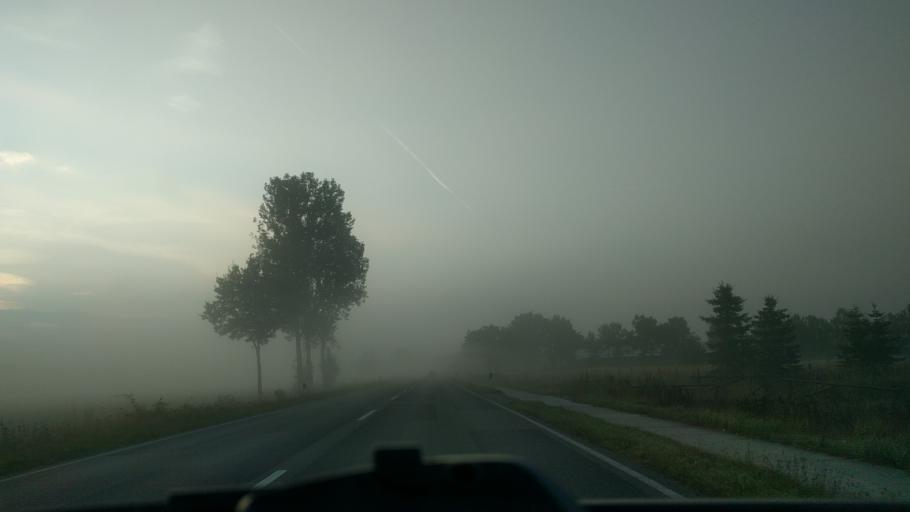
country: DE
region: Lower Saxony
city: Isenbuttel
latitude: 52.4536
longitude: 10.5820
